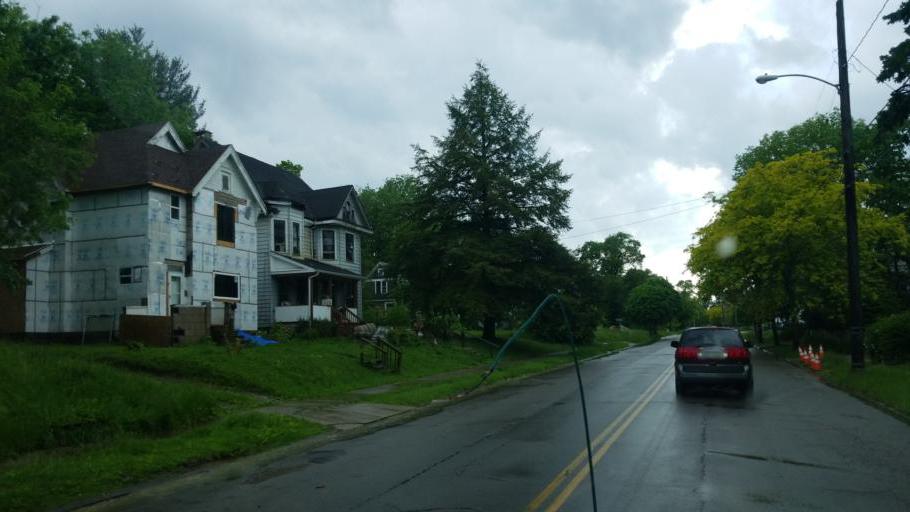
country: US
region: Ohio
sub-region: Richland County
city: Mansfield
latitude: 40.7633
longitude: -82.5243
